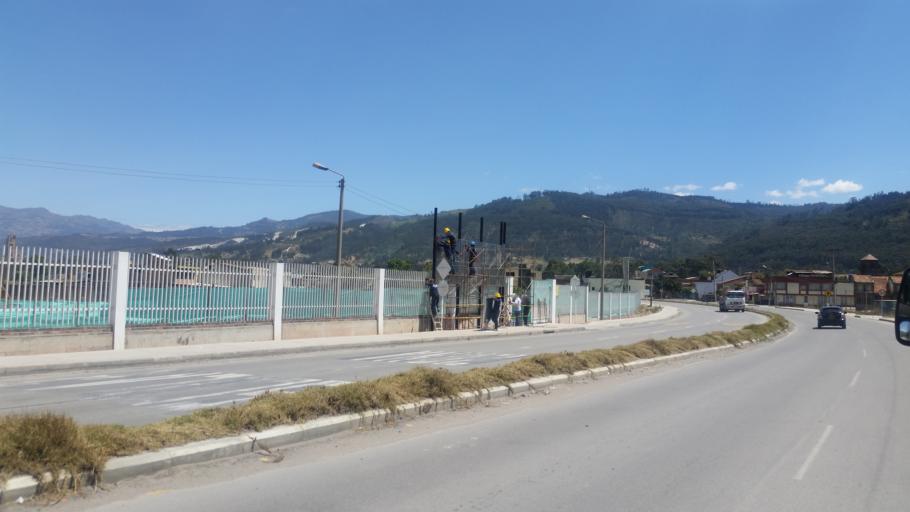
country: CO
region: Boyaca
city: Nobsa
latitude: 5.7579
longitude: -72.9061
